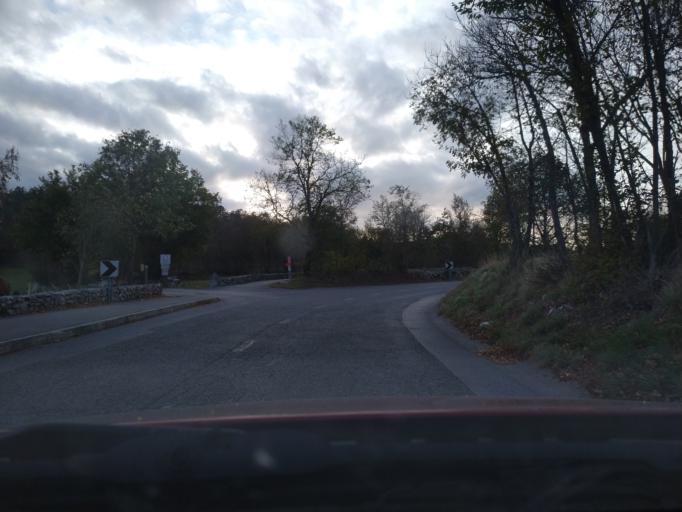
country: SI
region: Divaca
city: Divaca
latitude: 45.6615
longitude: 13.9875
